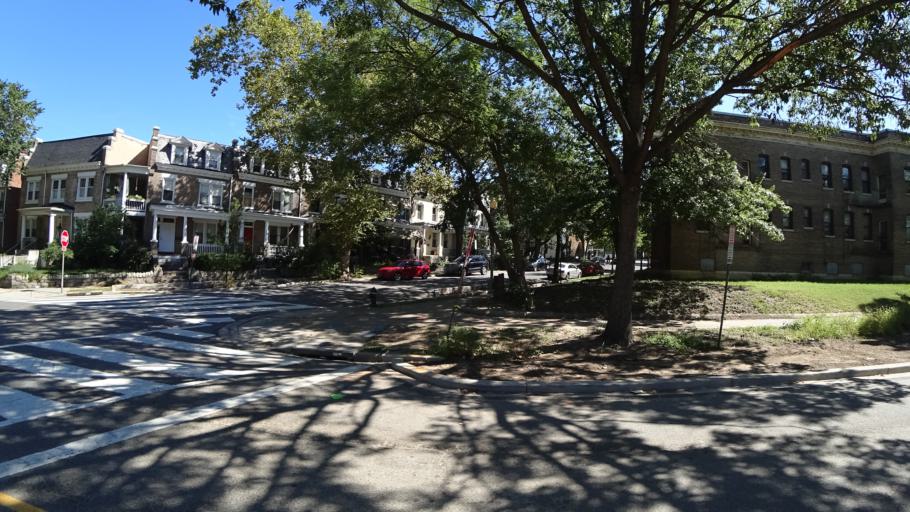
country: US
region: Maryland
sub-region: Montgomery County
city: Takoma Park
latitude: 38.9439
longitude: -77.0273
